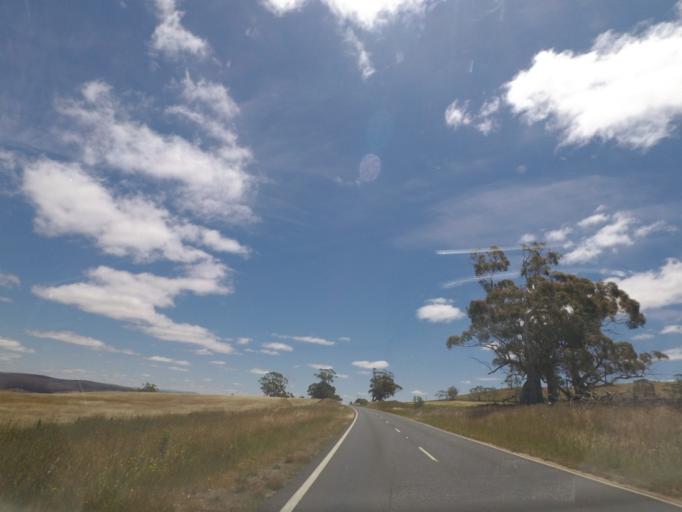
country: AU
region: Victoria
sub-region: Mount Alexander
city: Castlemaine
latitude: -37.2711
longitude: 144.1442
